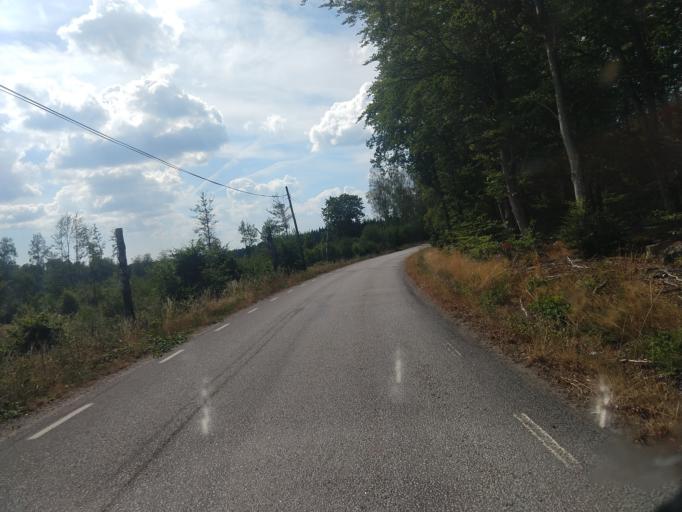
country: SE
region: Blekinge
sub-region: Karlskrona Kommun
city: Rodeby
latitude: 56.2385
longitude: 15.5693
